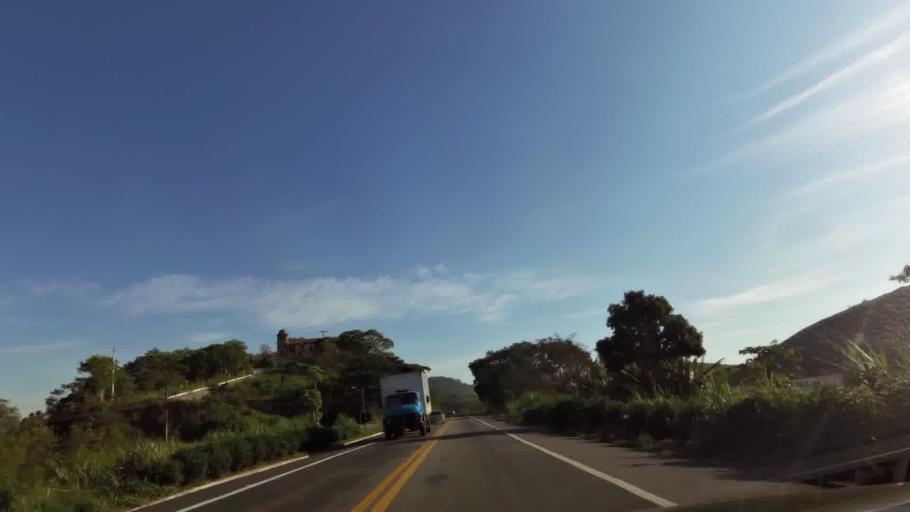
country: BR
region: Espirito Santo
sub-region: Viana
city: Viana
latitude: -20.4193
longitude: -40.4597
